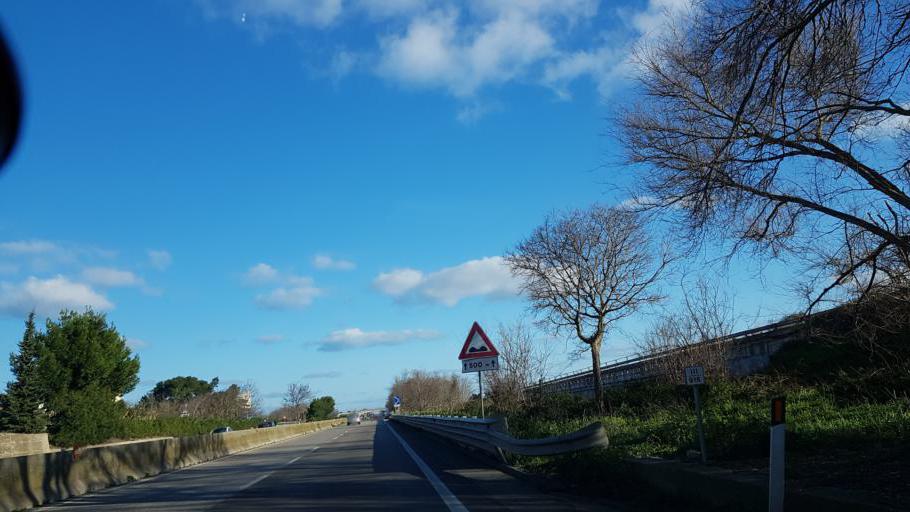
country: IT
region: Apulia
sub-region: Provincia di Brindisi
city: Brindisi
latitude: 40.6198
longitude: 17.9356
